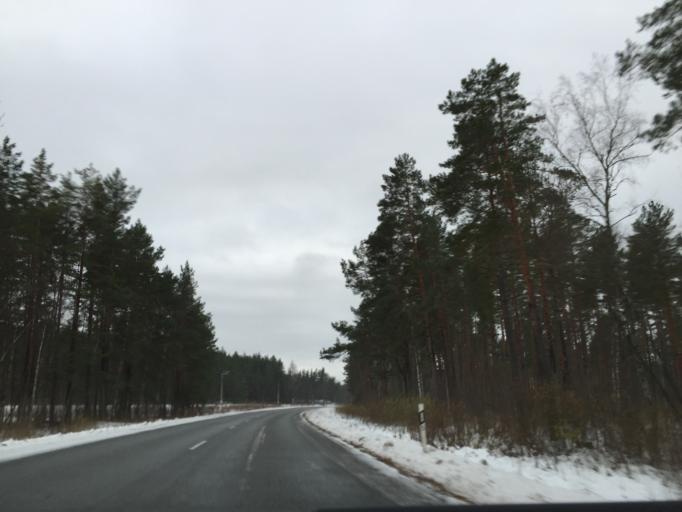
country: LV
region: Saulkrastu
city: Saulkrasti
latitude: 57.2090
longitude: 24.3808
